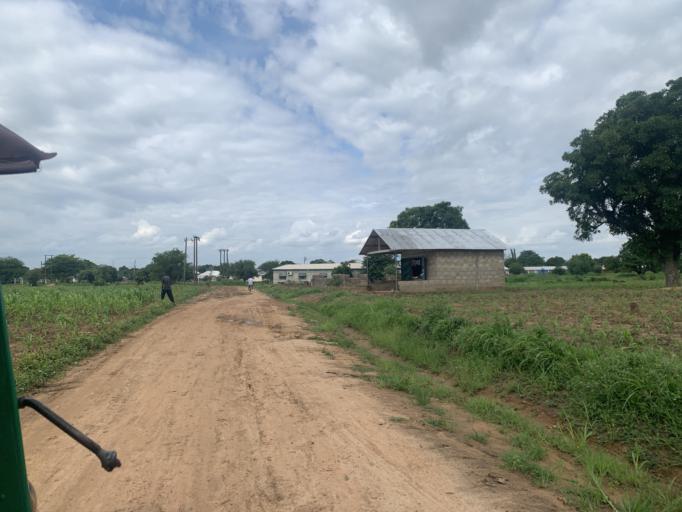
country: GH
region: Upper East
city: Navrongo
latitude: 10.8650
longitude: -1.0729
